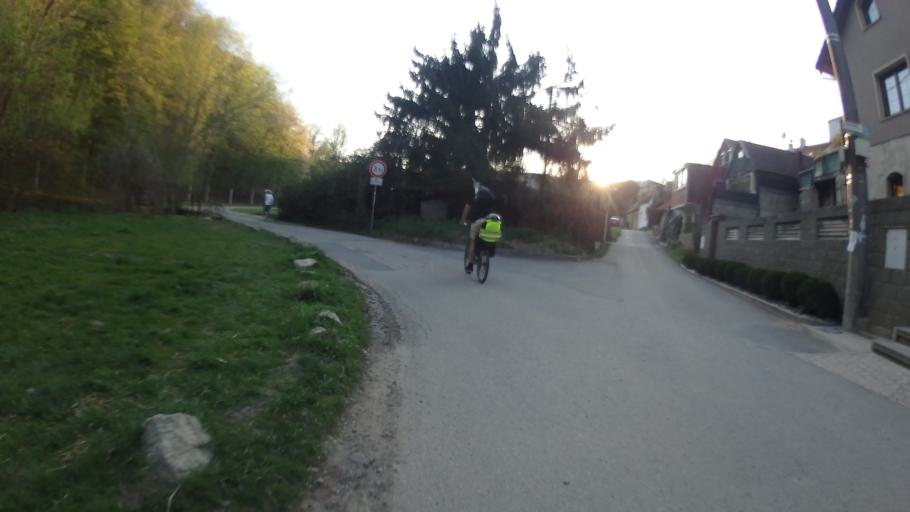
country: CZ
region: South Moravian
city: Troubsko
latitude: 49.2194
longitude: 16.5303
